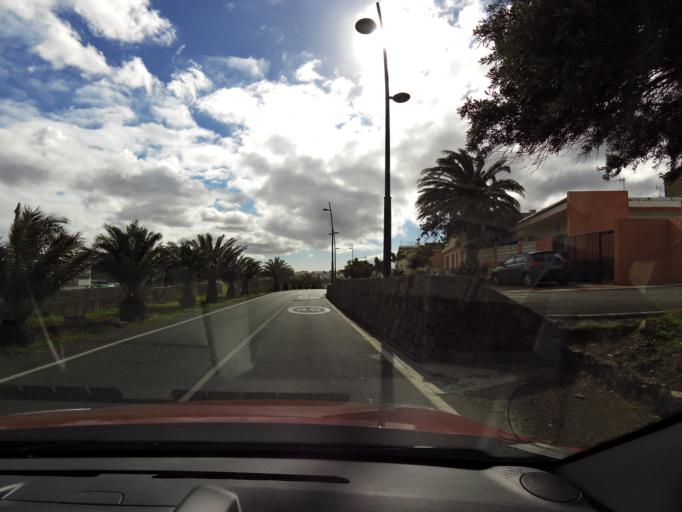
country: ES
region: Canary Islands
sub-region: Provincia de Las Palmas
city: Ingenio
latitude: 27.9130
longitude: -15.4399
